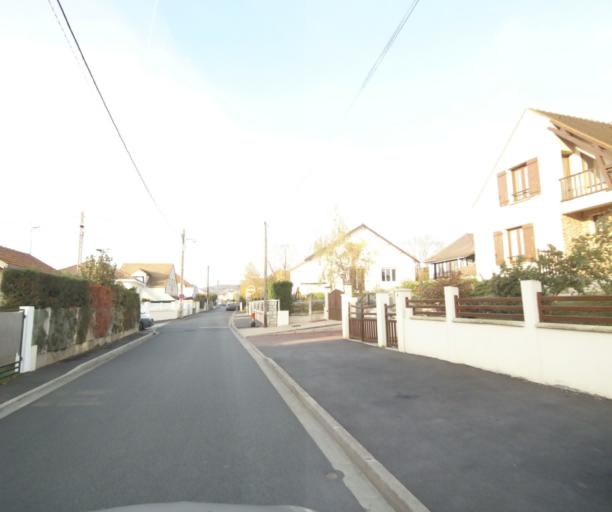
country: FR
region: Ile-de-France
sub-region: Departement des Yvelines
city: Triel-sur-Seine
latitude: 48.9716
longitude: 2.0101
